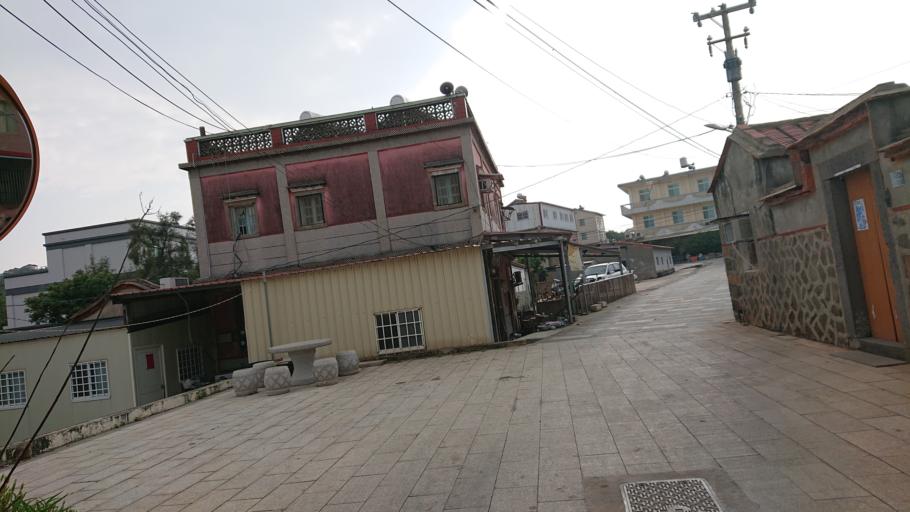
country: TW
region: Fukien
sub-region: Kinmen
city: Jincheng
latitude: 24.4467
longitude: 118.2530
